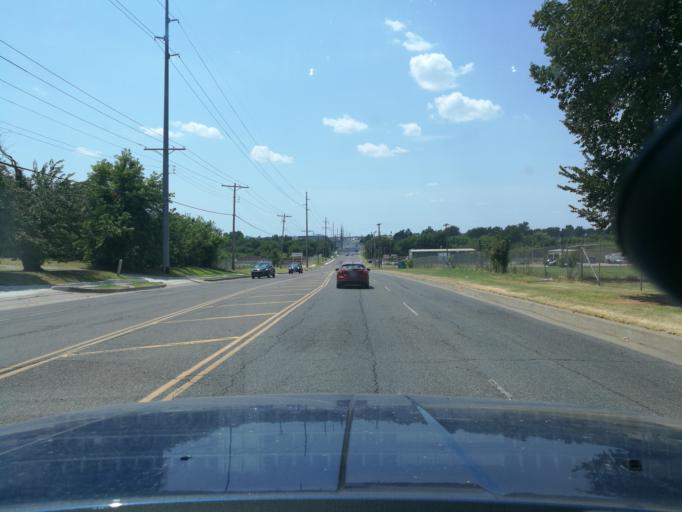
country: US
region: Oklahoma
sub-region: Oklahoma County
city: Del City
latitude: 35.4208
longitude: -97.4778
